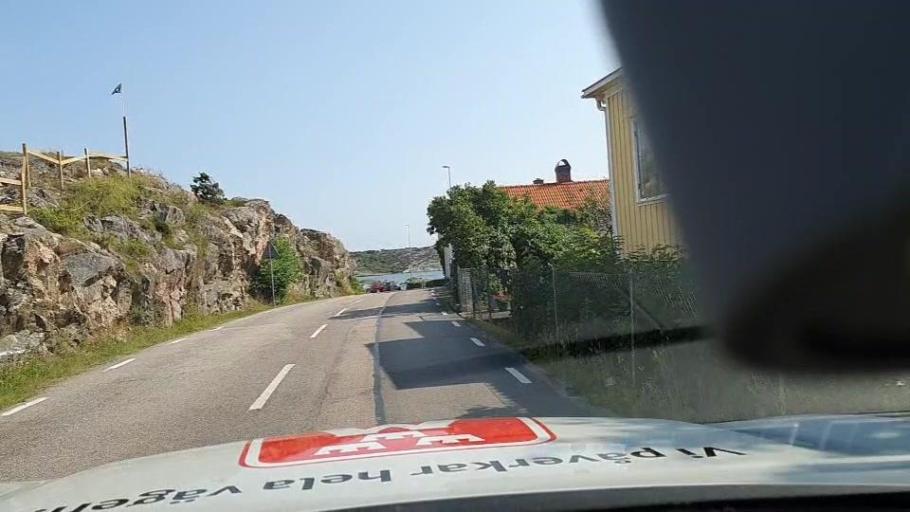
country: SE
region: Vaestra Goetaland
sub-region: Tjorns Kommun
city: Skaerhamn
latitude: 58.1086
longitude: 11.4671
